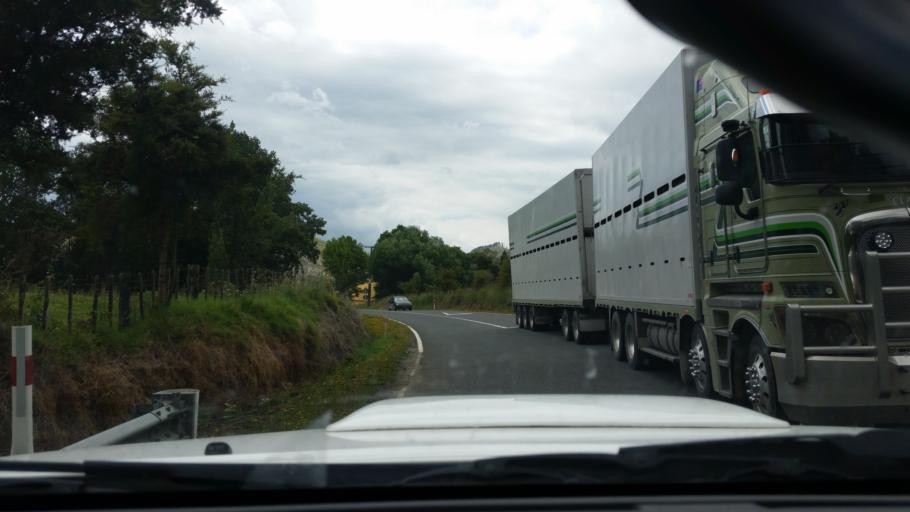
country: NZ
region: Northland
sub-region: Kaipara District
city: Dargaville
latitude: -35.7464
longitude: 173.8774
